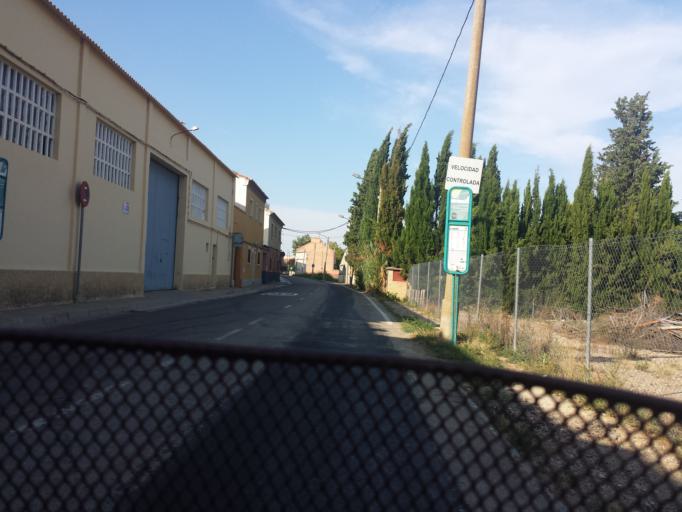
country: ES
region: Aragon
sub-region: Provincia de Zaragoza
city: Villanueva de Gallego
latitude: 41.7142
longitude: -0.8446
